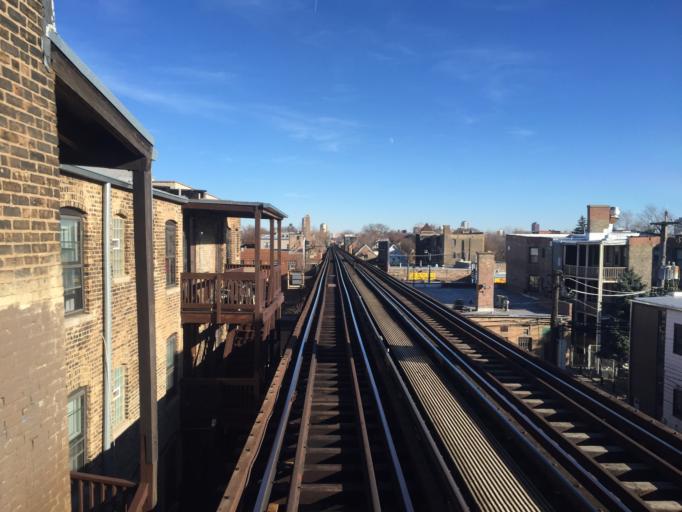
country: US
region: Illinois
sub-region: Cook County
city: Lincolnwood
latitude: 41.9437
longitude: -87.6696
